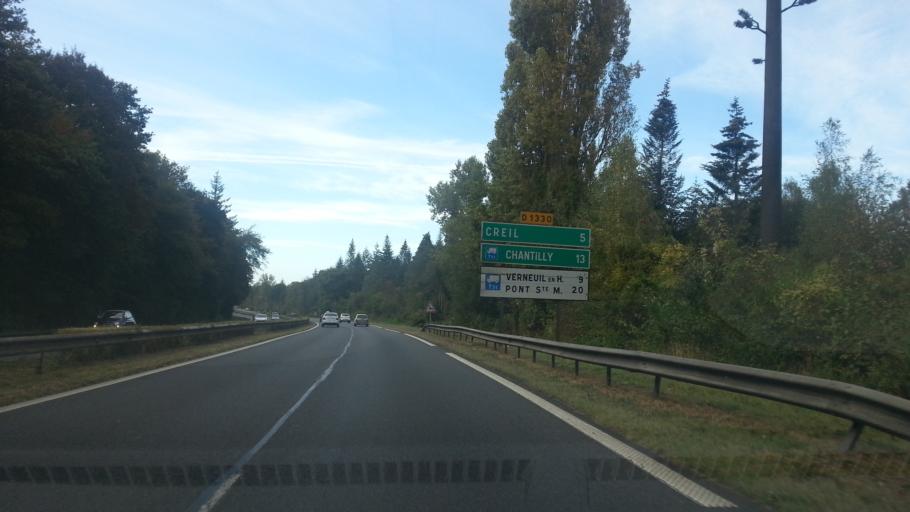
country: FR
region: Picardie
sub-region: Departement de l'Oise
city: Avilly-Saint-Leonard
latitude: 49.2353
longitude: 2.5338
